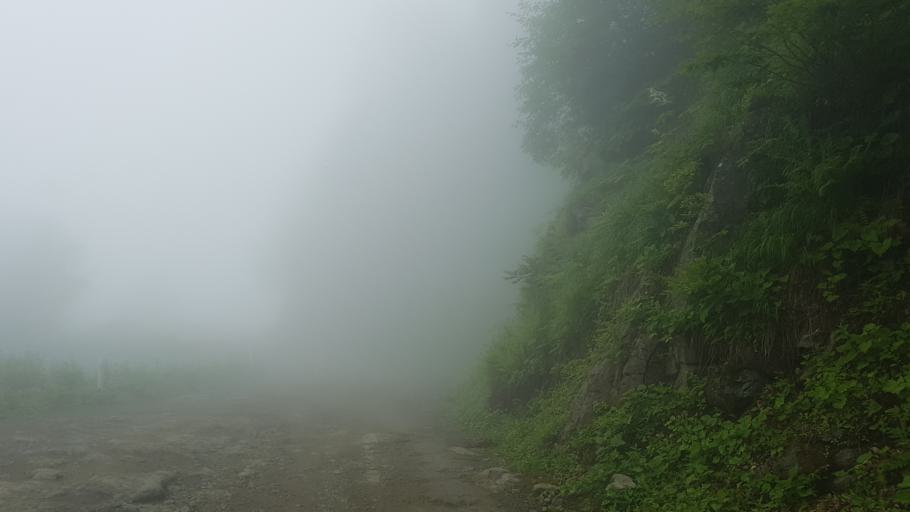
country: GE
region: Guria
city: Ozurgeti
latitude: 41.8297
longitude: 42.1482
